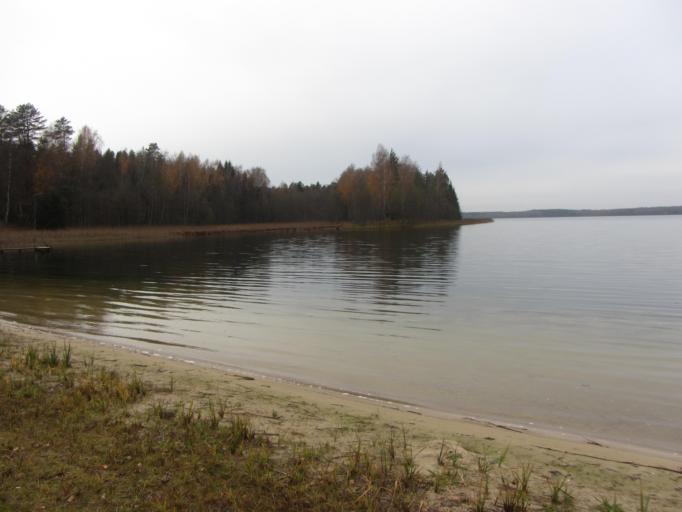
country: LT
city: Dukstas
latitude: 55.6014
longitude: 26.3157
